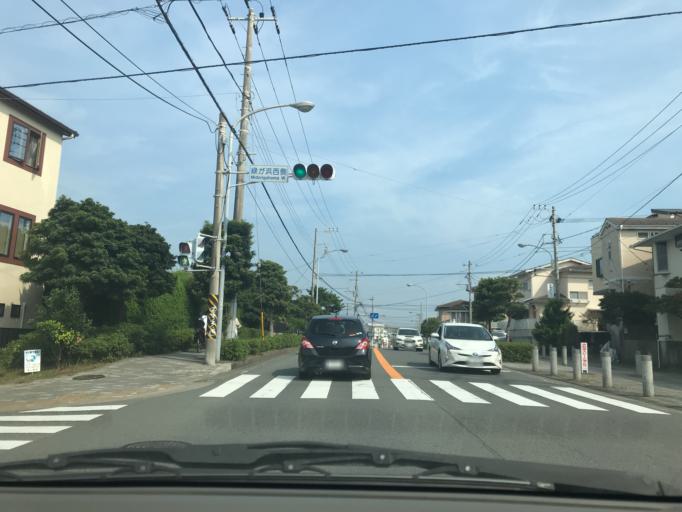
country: JP
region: Kanagawa
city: Chigasaki
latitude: 35.3256
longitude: 139.4354
